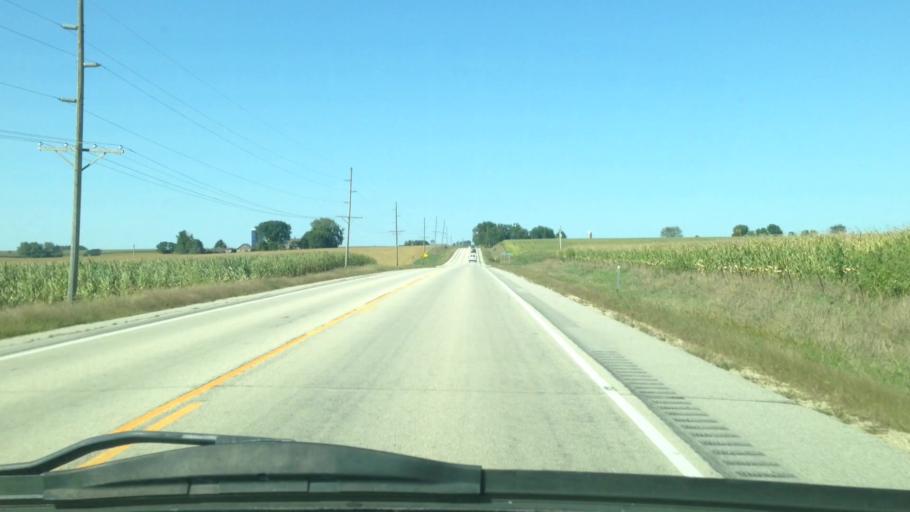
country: US
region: Minnesota
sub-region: Fillmore County
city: Rushford
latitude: 43.9023
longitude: -91.7401
